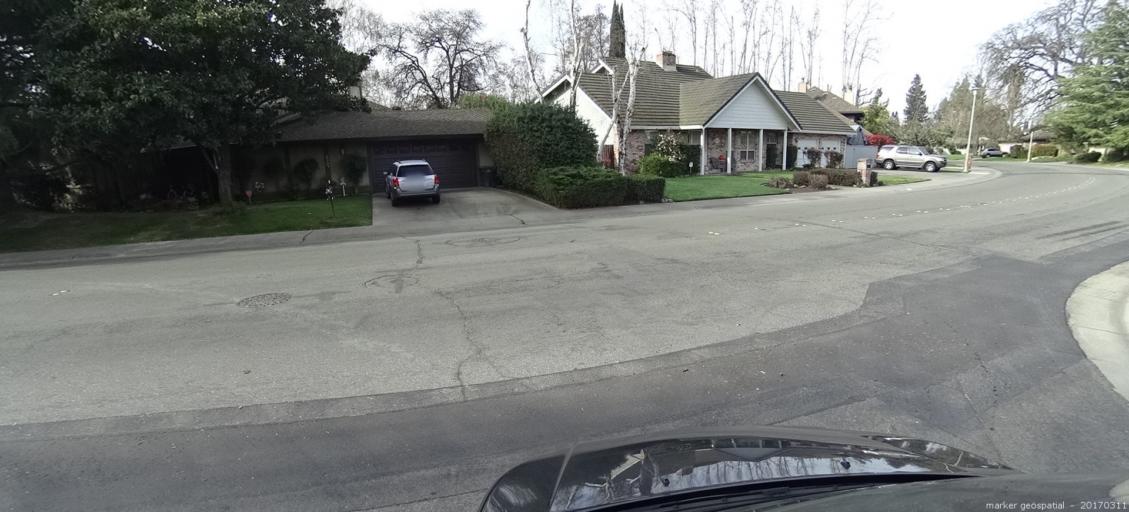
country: US
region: California
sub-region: Yolo County
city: West Sacramento
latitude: 38.5103
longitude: -121.5471
